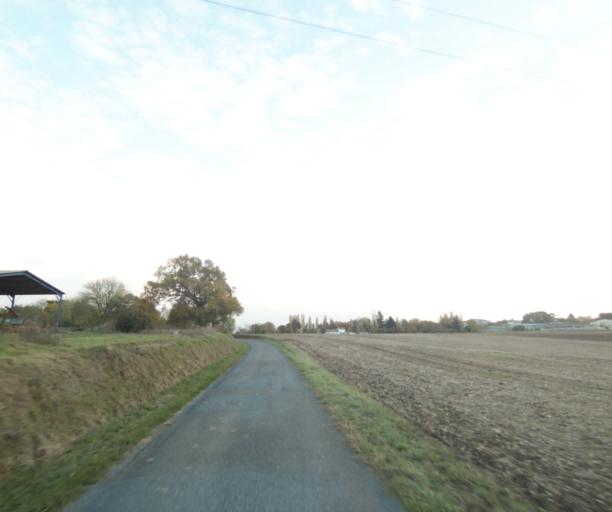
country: FR
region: Poitou-Charentes
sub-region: Departement de la Charente-Maritime
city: Saintes
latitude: 45.7647
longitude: -0.6488
